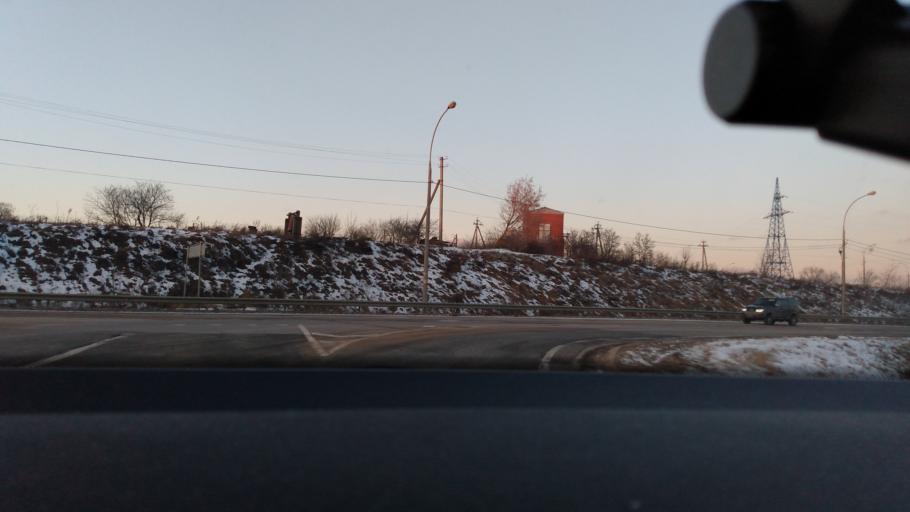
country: RU
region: Moskovskaya
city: Kolomna
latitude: 55.0883
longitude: 38.9036
